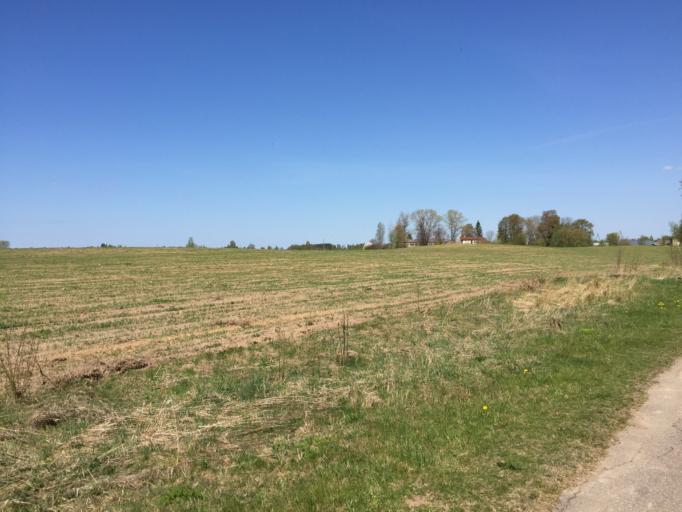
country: LV
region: Saulkrastu
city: Saulkrasti
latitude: 57.3265
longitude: 24.4882
